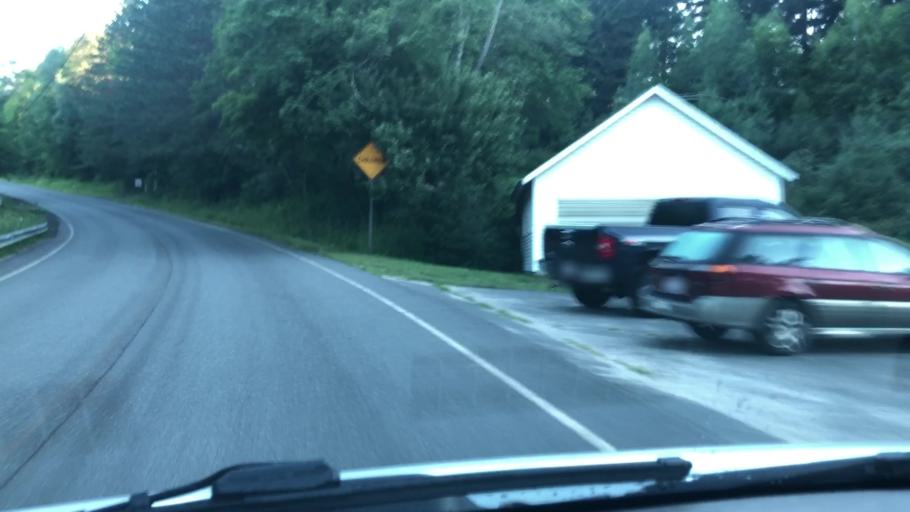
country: US
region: Massachusetts
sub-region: Berkshire County
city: Hinsdale
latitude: 42.4790
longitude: -72.9851
